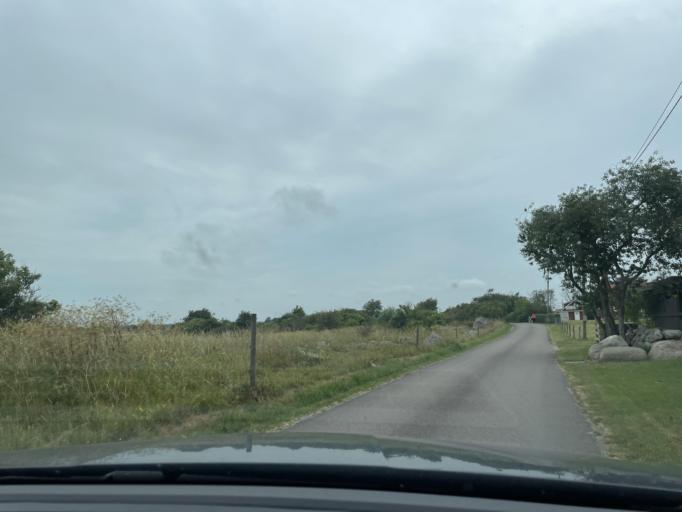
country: SE
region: Skane
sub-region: Bromolla Kommun
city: Bromoella
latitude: 55.9982
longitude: 14.4447
